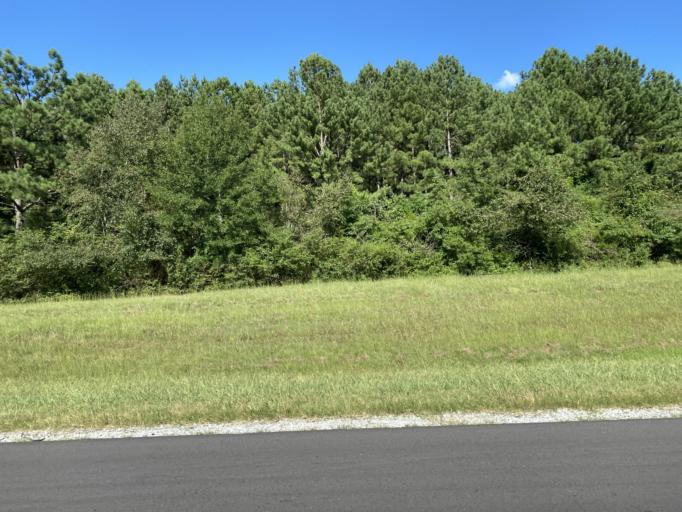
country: US
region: Alabama
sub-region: Limestone County
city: Athens
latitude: 34.7600
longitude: -86.9384
